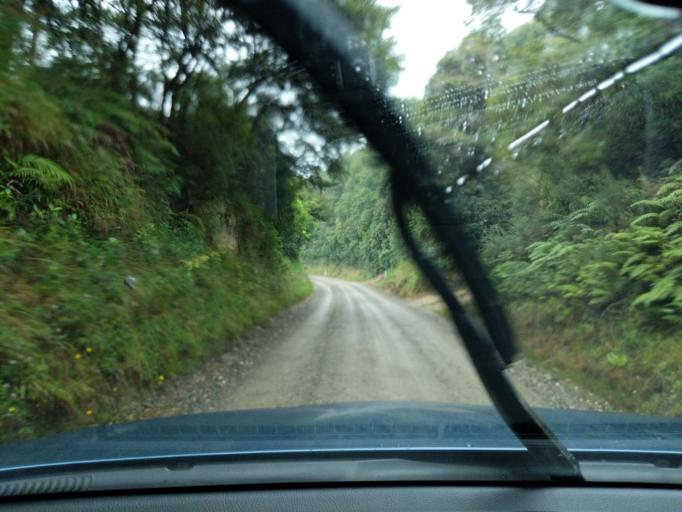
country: NZ
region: Tasman
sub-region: Tasman District
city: Takaka
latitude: -40.6301
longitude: 172.4917
